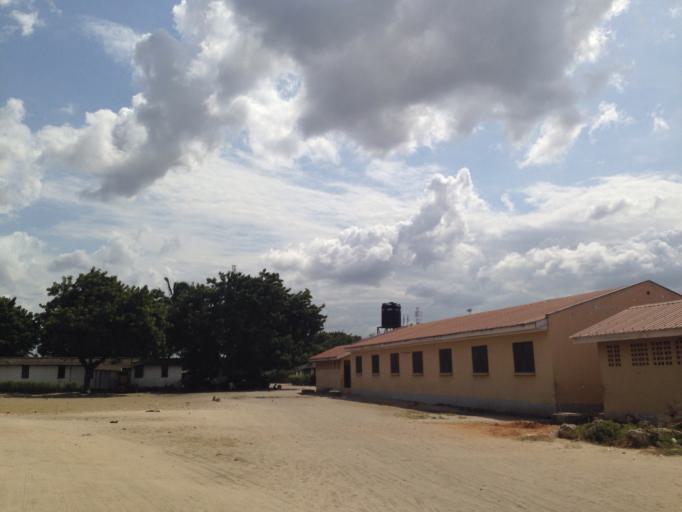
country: TZ
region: Dar es Salaam
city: Dar es Salaam
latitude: -6.8428
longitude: 39.2823
